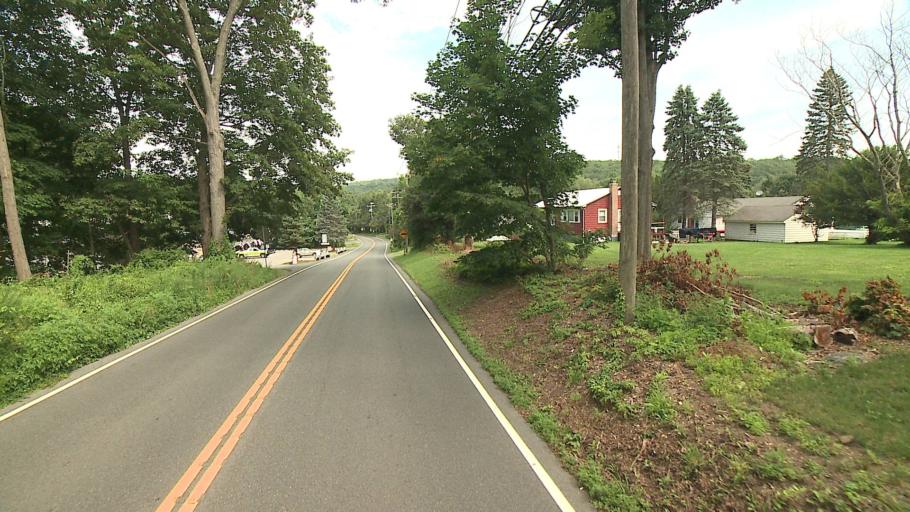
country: US
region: Connecticut
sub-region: Fairfield County
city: Sherman
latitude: 41.5062
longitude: -73.4701
